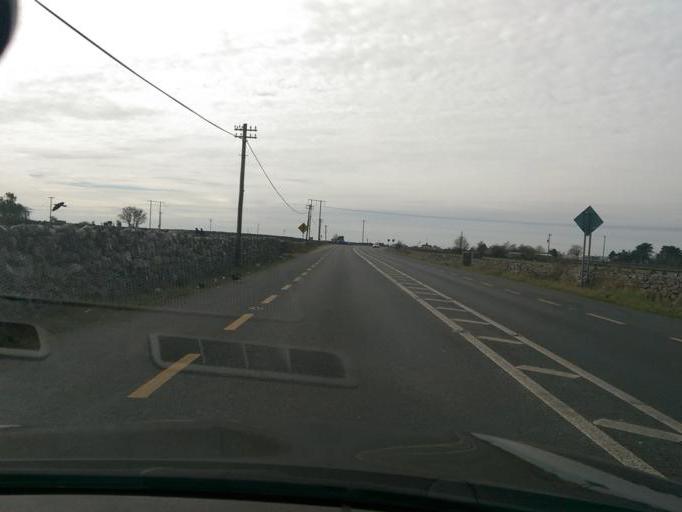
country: IE
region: Connaught
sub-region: County Galway
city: Claregalway
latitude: 53.3643
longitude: -8.9096
